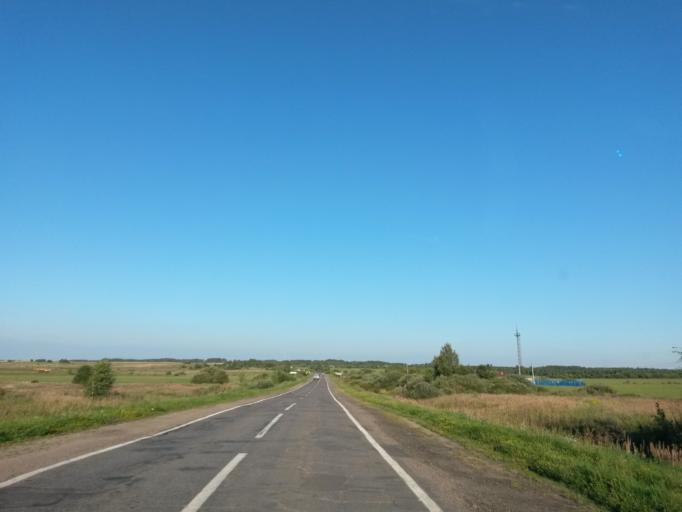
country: RU
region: Jaroslavl
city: Gavrilov-Yam
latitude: 57.3081
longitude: 39.8767
